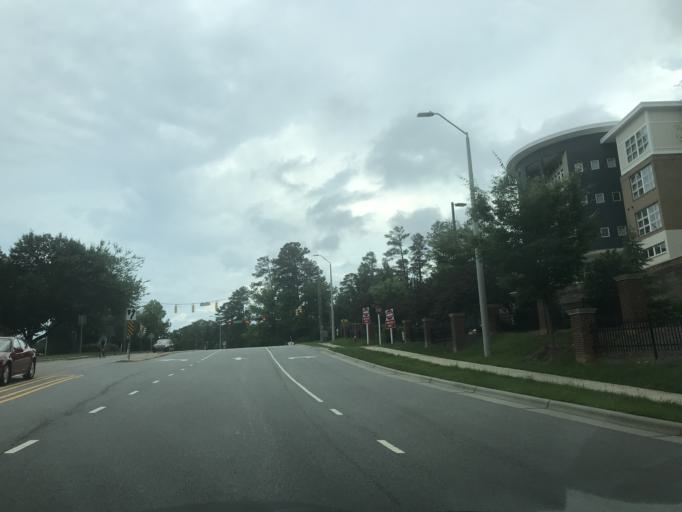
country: US
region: North Carolina
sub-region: Wake County
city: Cary
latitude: 35.7712
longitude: -78.8063
